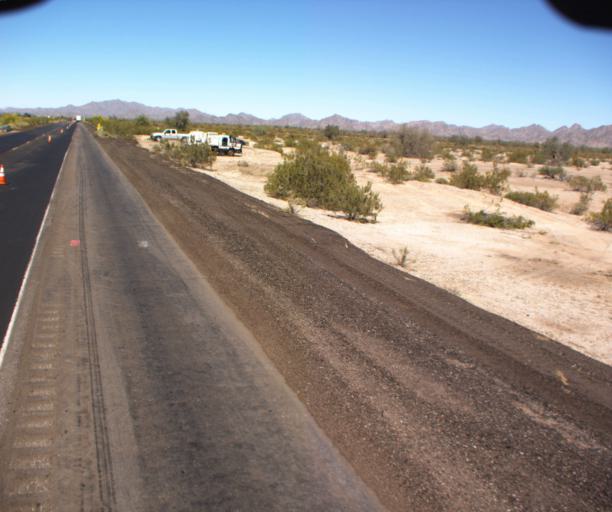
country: US
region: Arizona
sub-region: Maricopa County
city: Gila Bend
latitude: 33.0253
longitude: -112.6487
